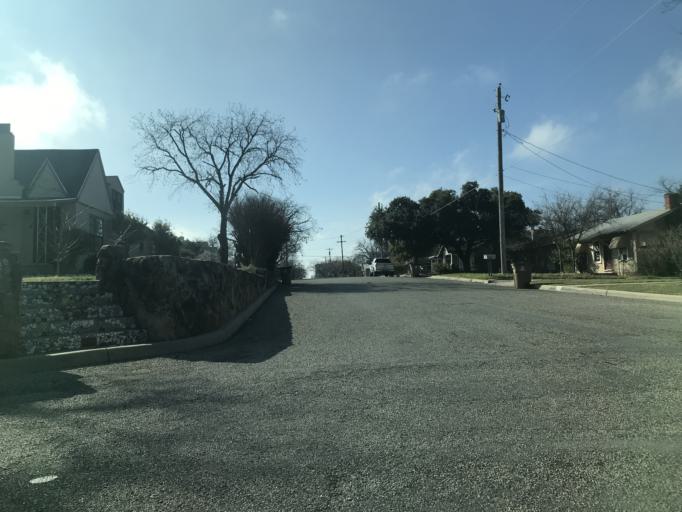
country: US
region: Texas
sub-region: Tom Green County
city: San Angelo
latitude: 31.4487
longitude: -100.4584
